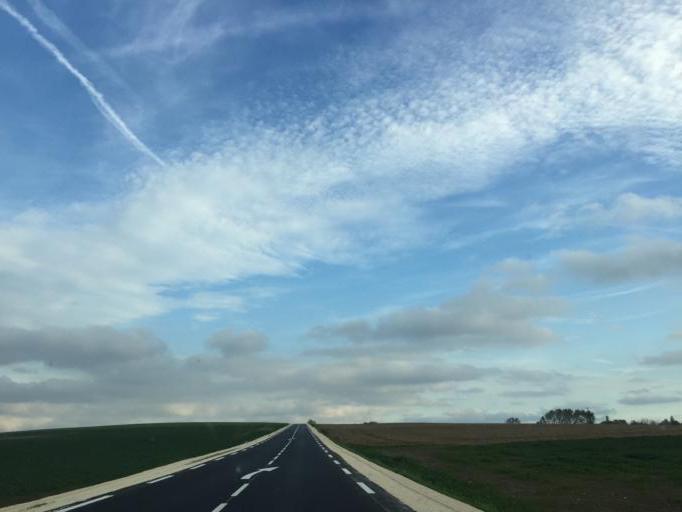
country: FR
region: Ile-de-France
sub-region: Departement de Seine-et-Marne
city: Saints
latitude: 48.6978
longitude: 3.0697
